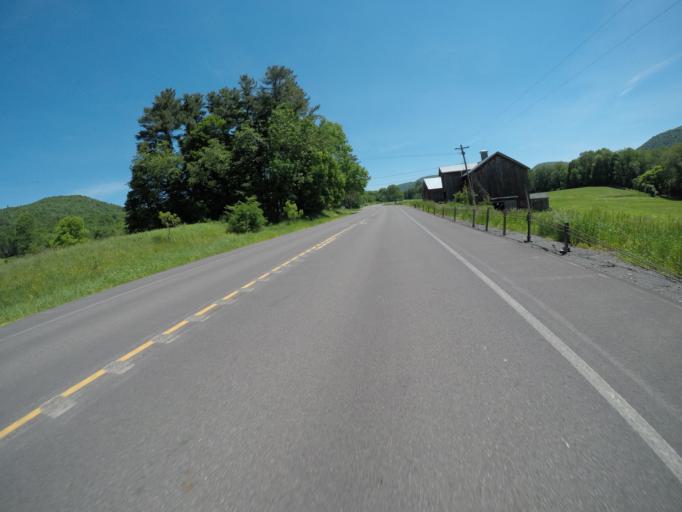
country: US
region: New York
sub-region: Delaware County
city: Walton
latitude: 42.1694
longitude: -75.0337
